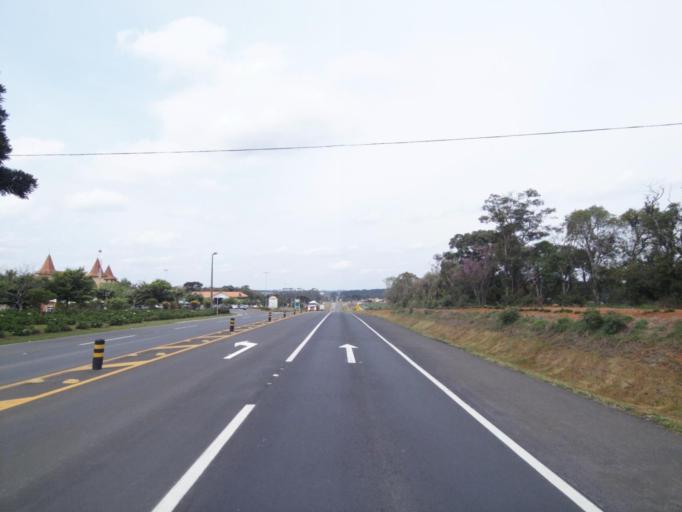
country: BR
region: Parana
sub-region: Irati
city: Irati
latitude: -25.4645
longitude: -50.5697
